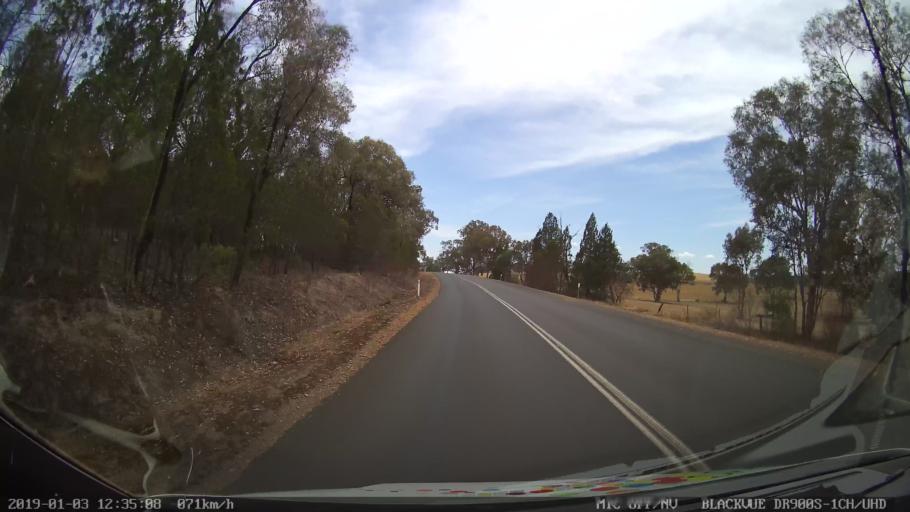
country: AU
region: New South Wales
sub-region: Weddin
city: Grenfell
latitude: -33.8697
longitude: 148.1688
